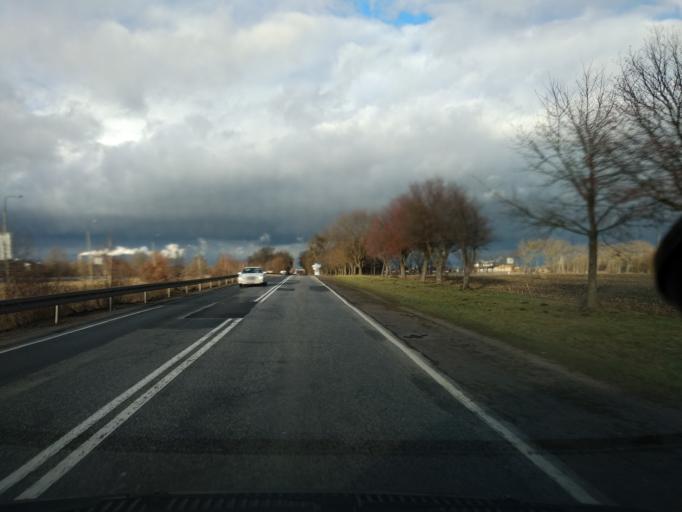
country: PL
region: Greater Poland Voivodeship
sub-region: Konin
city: Konin
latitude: 52.2594
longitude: 18.2683
